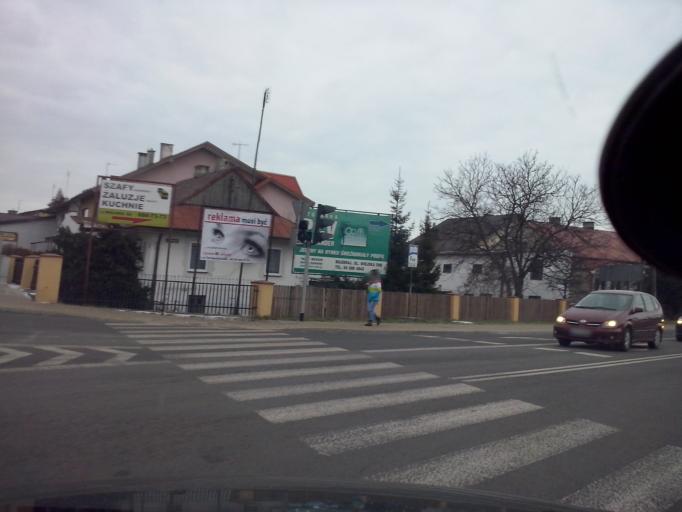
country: PL
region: Lublin Voivodeship
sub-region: Powiat bilgorajski
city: Bilgoraj
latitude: 50.5254
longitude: 22.7131
